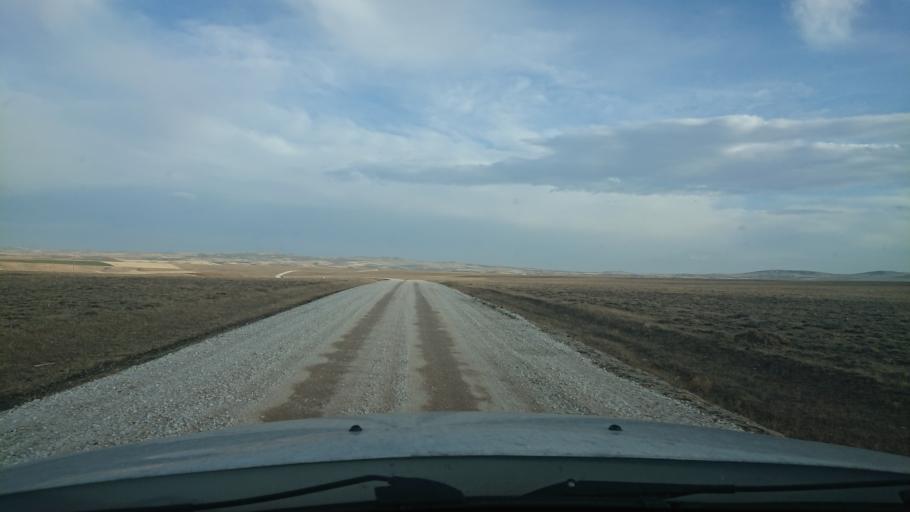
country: TR
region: Aksaray
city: Agacoren
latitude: 38.7271
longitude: 33.8684
